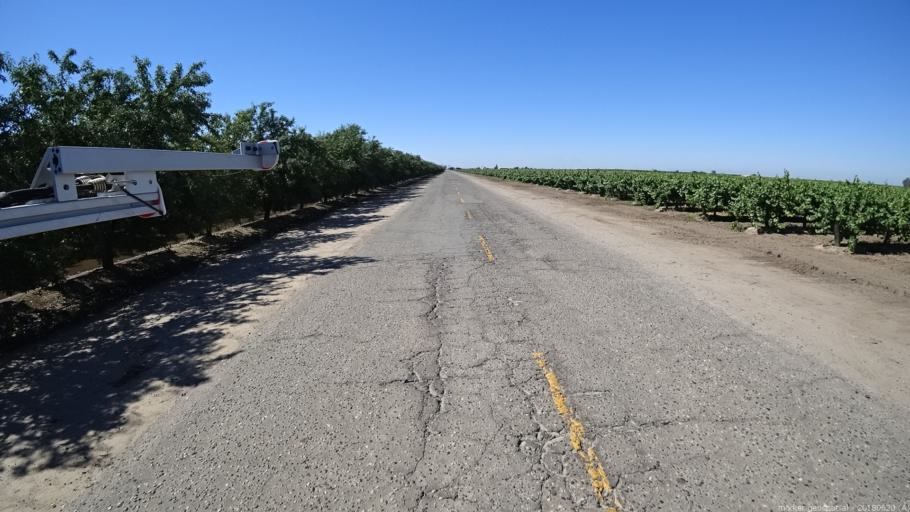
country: US
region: California
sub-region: Madera County
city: Parkwood
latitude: 36.9054
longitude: -120.0285
